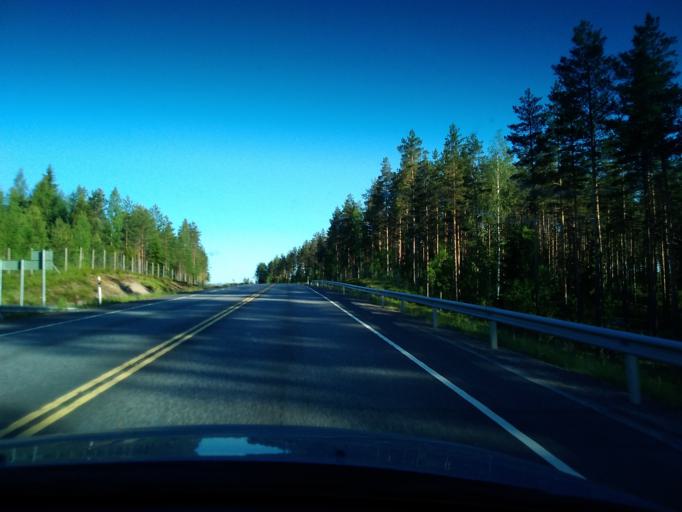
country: FI
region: Uusimaa
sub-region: Helsinki
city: Karkkila
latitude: 60.5868
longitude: 24.1224
